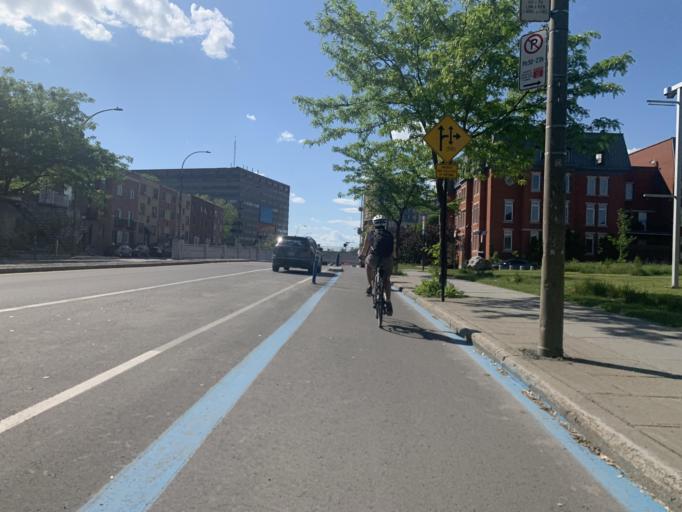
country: CA
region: Quebec
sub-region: Montreal
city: Montreal
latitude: 45.5294
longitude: -73.5948
